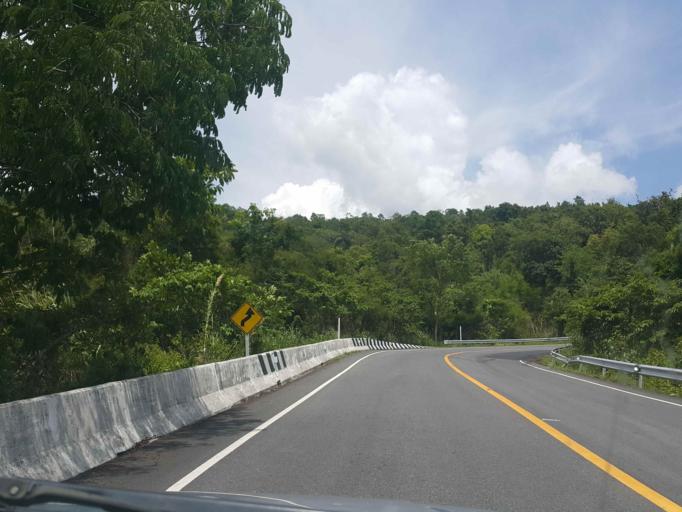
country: TH
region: Phayao
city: Chiang Muan
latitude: 18.8434
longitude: 100.3509
